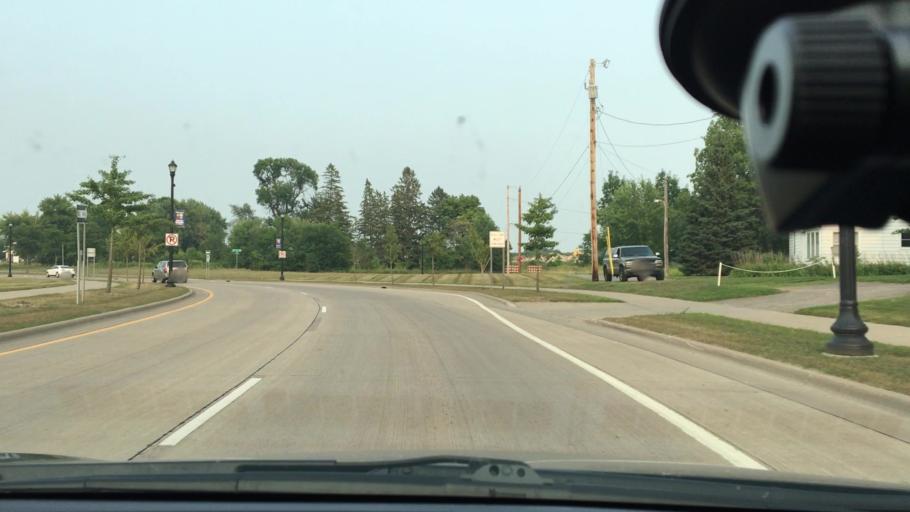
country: US
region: Minnesota
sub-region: Wright County
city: Saint Michael
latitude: 45.2087
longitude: -93.6628
